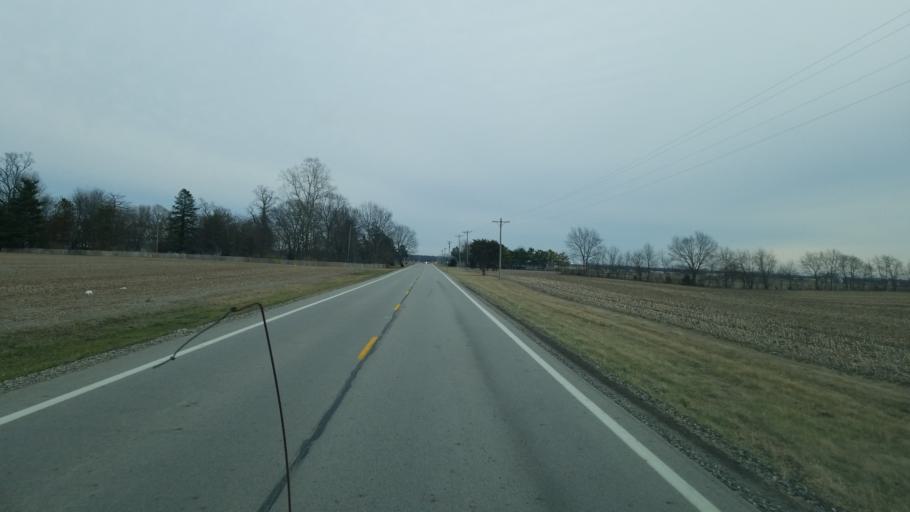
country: US
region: Ohio
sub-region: Pickaway County
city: Circleville
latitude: 39.6078
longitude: -82.9979
